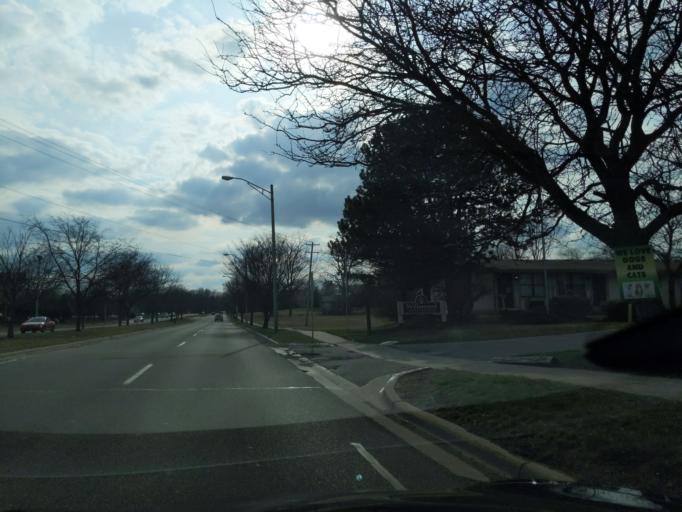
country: US
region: Michigan
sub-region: Ingham County
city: Holt
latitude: 42.6623
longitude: -84.5510
